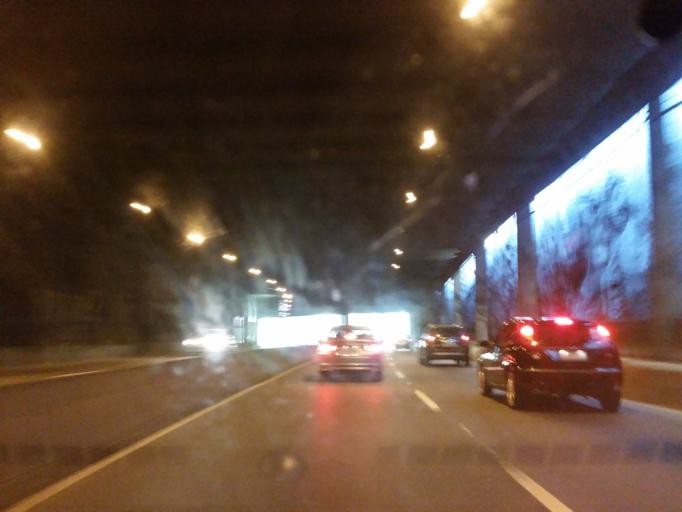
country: BR
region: Rio de Janeiro
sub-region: Rio De Janeiro
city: Rio de Janeiro
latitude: -22.9802
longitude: -43.2314
